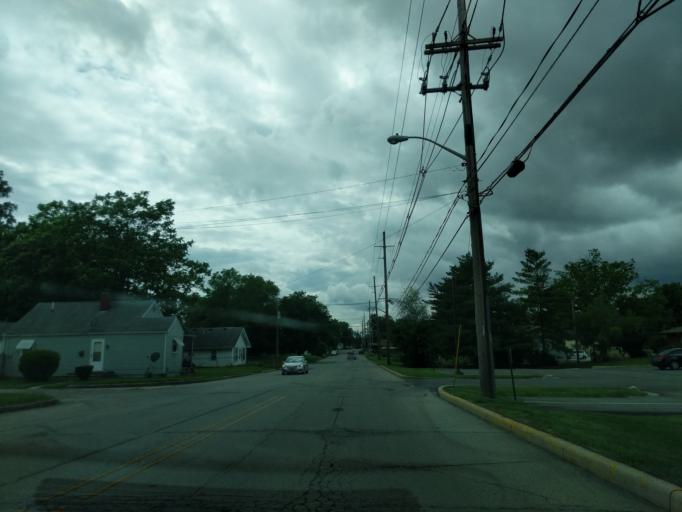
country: US
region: Indiana
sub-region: Madison County
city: Anderson
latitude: 40.0974
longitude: -85.6834
